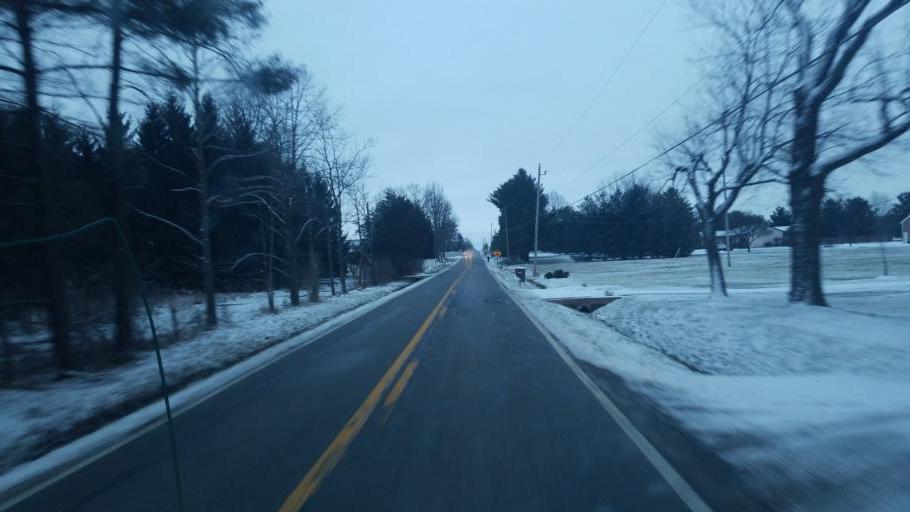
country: US
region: Ohio
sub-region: Delaware County
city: Sunbury
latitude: 40.1873
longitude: -82.8294
